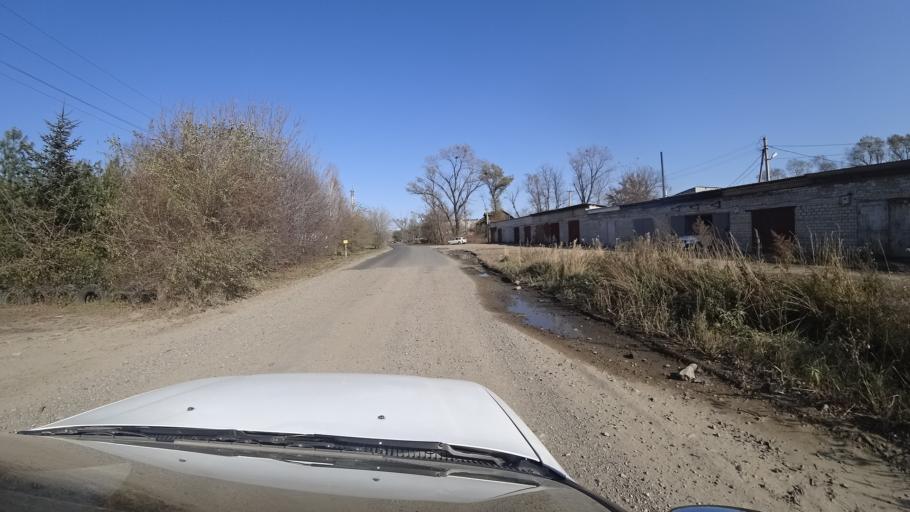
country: RU
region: Primorskiy
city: Dal'nerechensk
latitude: 45.9336
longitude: 133.7206
